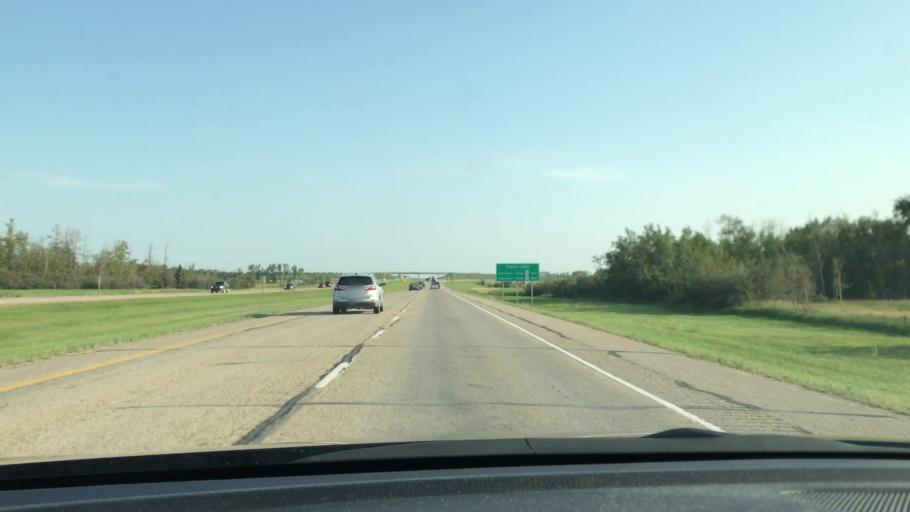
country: CA
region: Alberta
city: Millet
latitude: 53.0999
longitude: -113.5984
